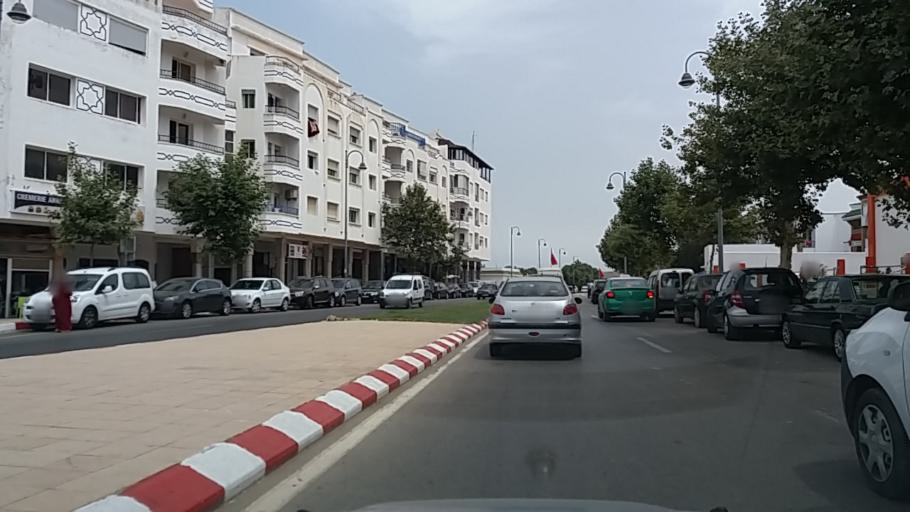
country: MA
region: Tanger-Tetouan
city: Asilah
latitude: 35.4699
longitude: -6.0297
